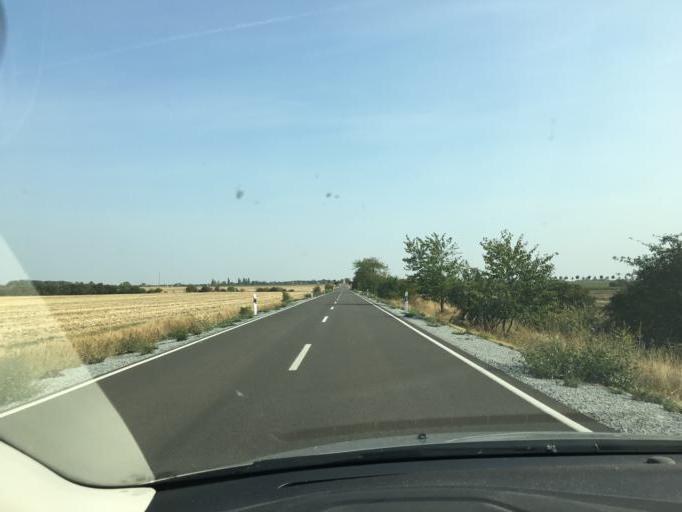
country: DE
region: Saxony-Anhalt
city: Baalberge
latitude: 51.7991
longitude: 11.8589
